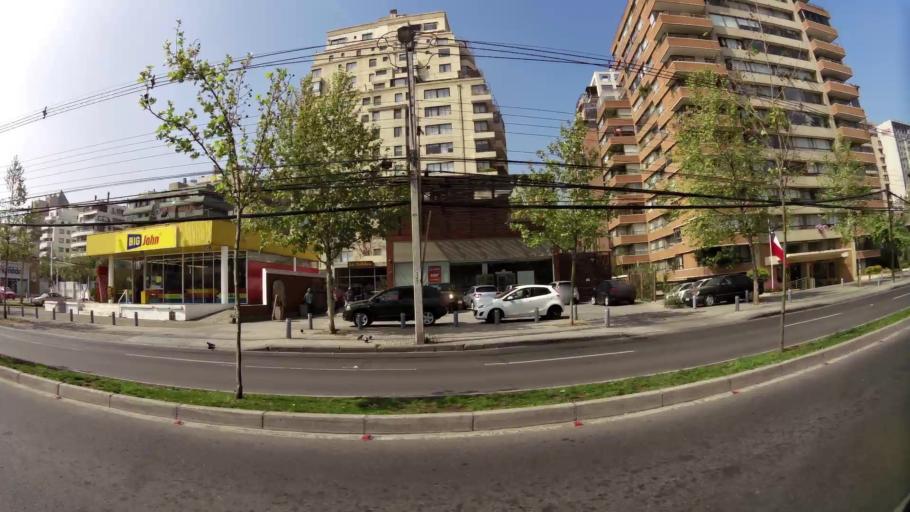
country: CL
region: Santiago Metropolitan
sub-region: Provincia de Santiago
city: Villa Presidente Frei, Nunoa, Santiago, Chile
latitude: -33.4053
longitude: -70.5977
